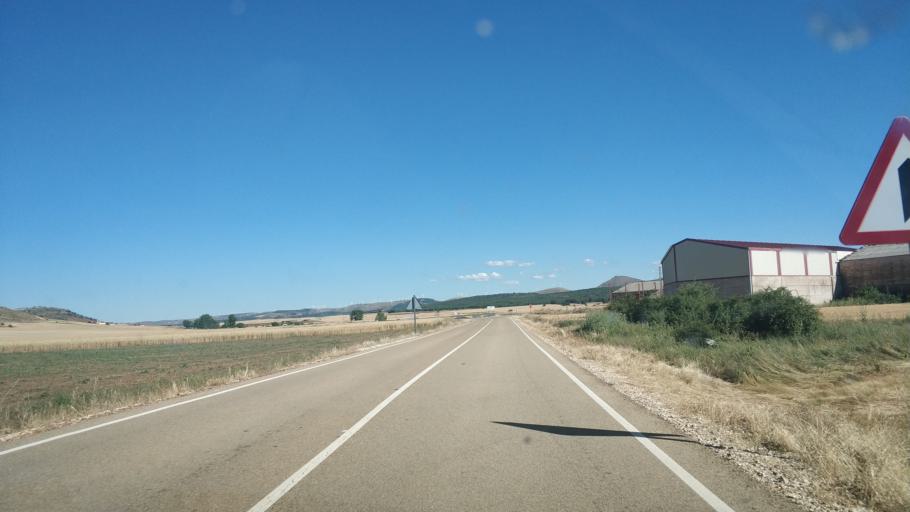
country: ES
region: Castille and Leon
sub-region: Provincia de Soria
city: Montejo de Tiermes
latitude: 41.3683
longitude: -3.1954
